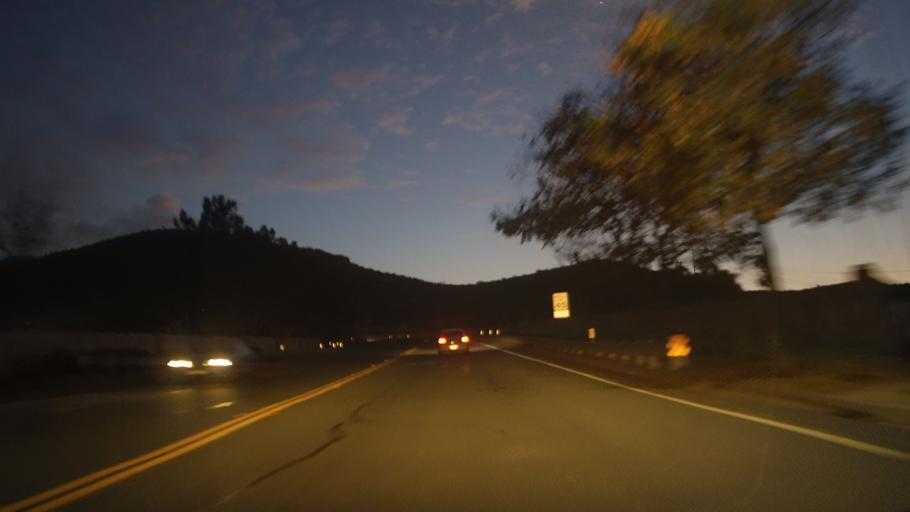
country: US
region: California
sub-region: San Diego County
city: Rancho San Diego
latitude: 32.7364
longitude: -116.9144
